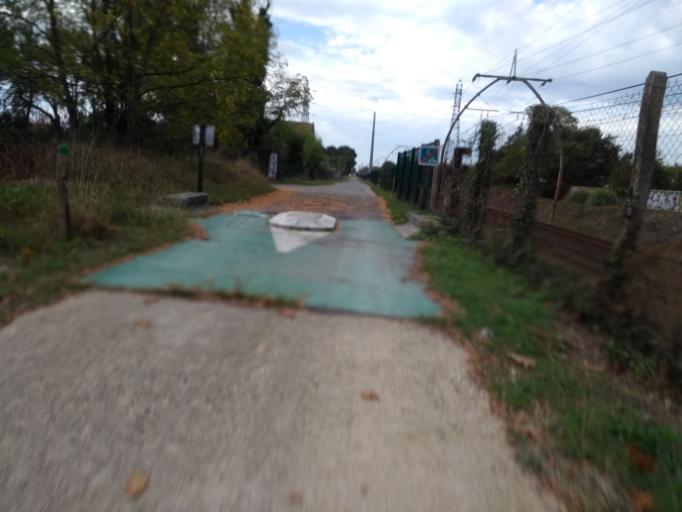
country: FR
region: Aquitaine
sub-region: Departement de la Gironde
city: Pessac
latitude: 44.7903
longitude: -0.6651
